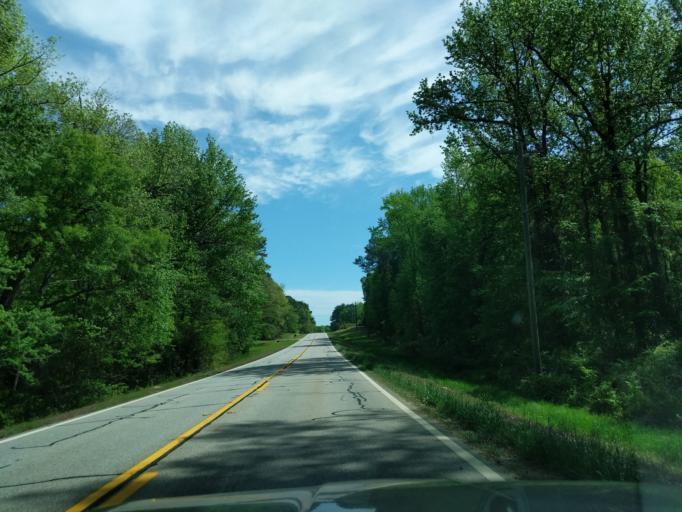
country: US
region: Georgia
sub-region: Columbia County
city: Appling
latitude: 33.6089
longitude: -82.3719
